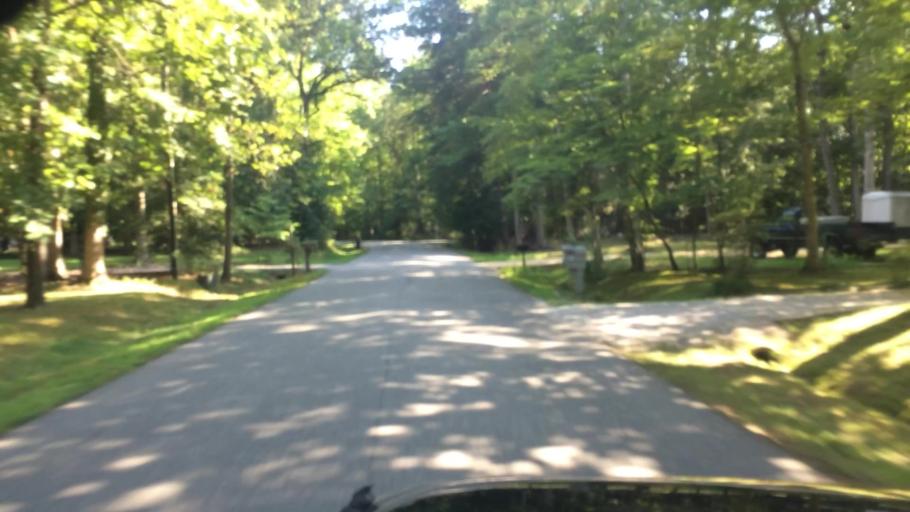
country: US
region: Virginia
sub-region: James City County
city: Williamsburg
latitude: 37.2447
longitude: -76.7978
